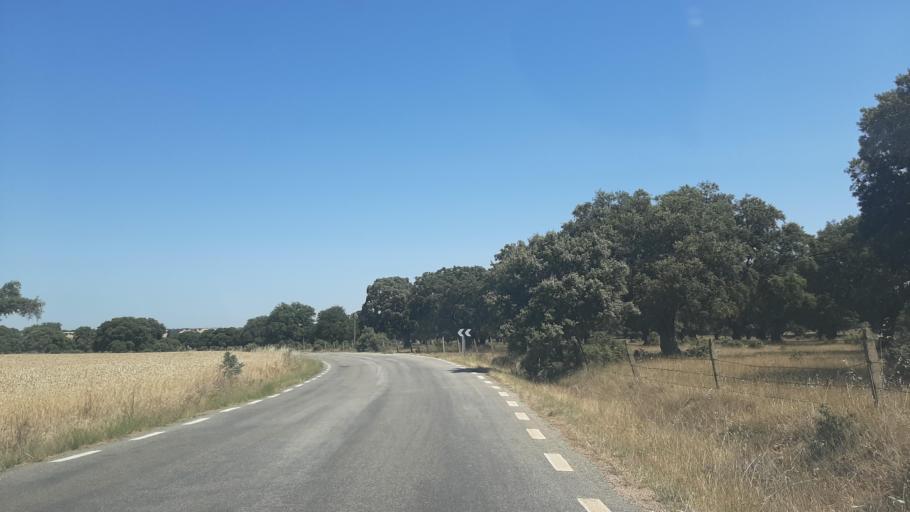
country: ES
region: Castille and Leon
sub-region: Provincia de Salamanca
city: Cabrillas
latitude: 40.7257
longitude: -6.1758
